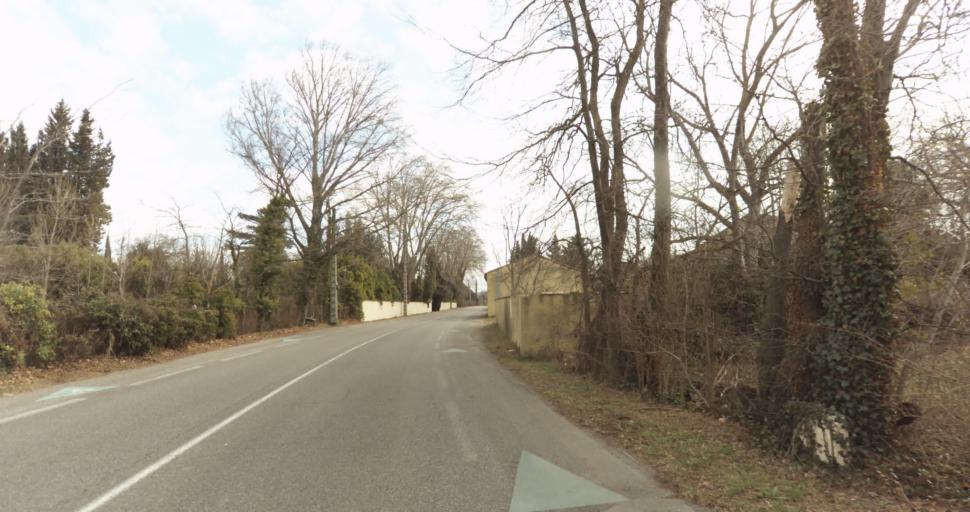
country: FR
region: Provence-Alpes-Cote d'Azur
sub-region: Departement du Vaucluse
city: Montfavet
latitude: 43.9377
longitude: 4.8858
